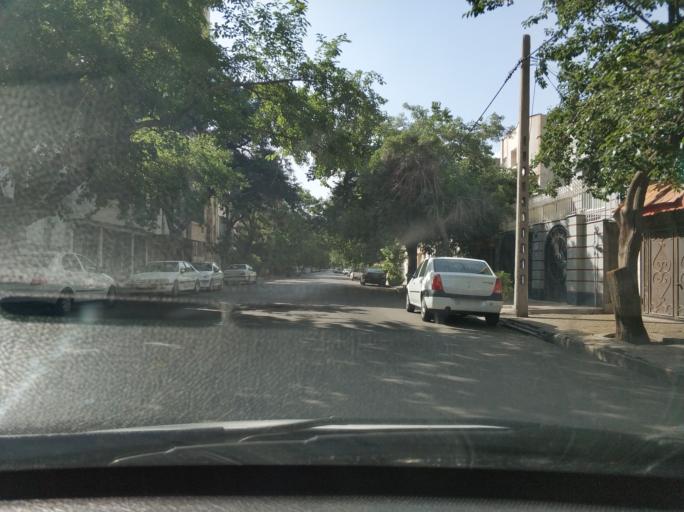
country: IR
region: Razavi Khorasan
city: Mashhad
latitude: 36.2709
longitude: 59.5989
